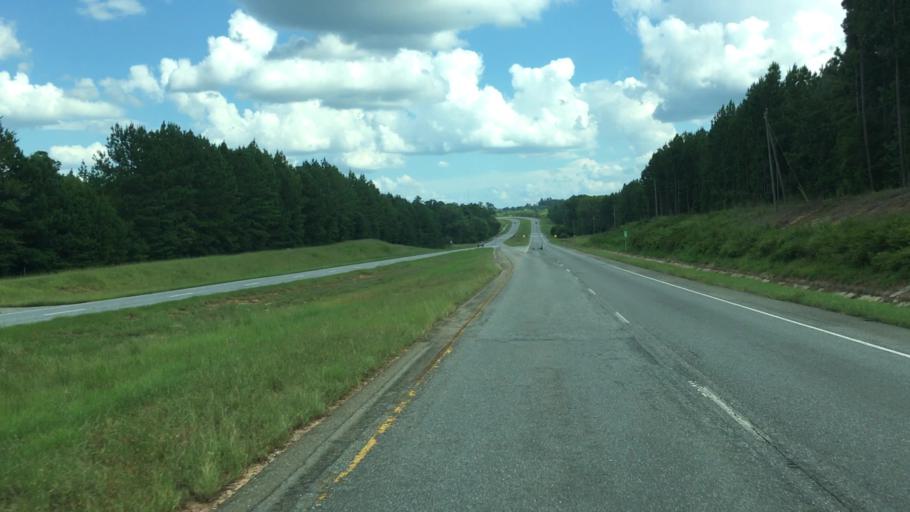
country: US
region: Georgia
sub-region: Wilkinson County
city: Irwinton
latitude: 32.7033
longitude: -83.1262
